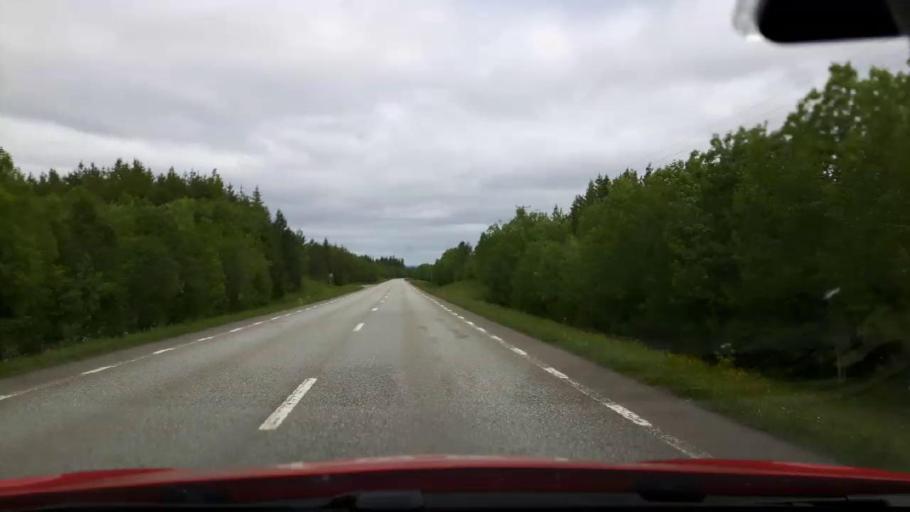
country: SE
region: Jaemtland
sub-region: Krokoms Kommun
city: Krokom
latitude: 63.5589
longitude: 14.6043
